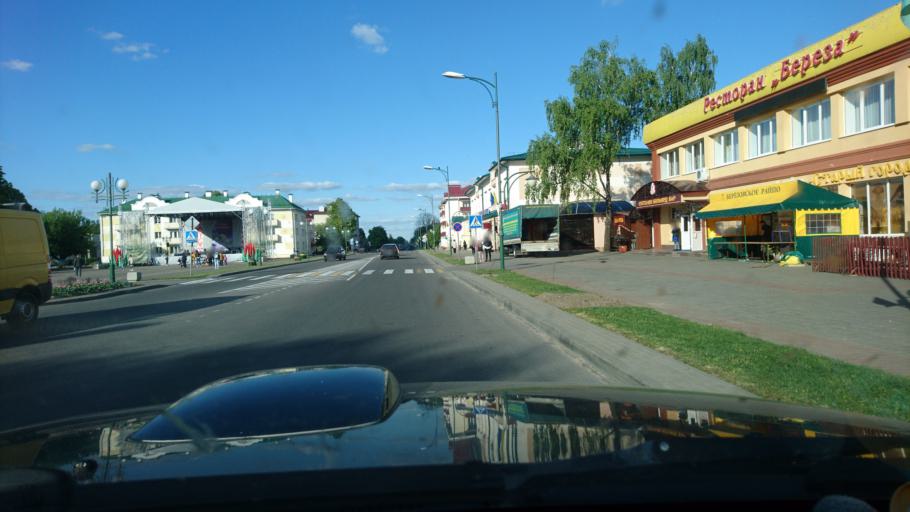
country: BY
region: Brest
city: Byaroza
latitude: 52.5340
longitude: 24.9842
